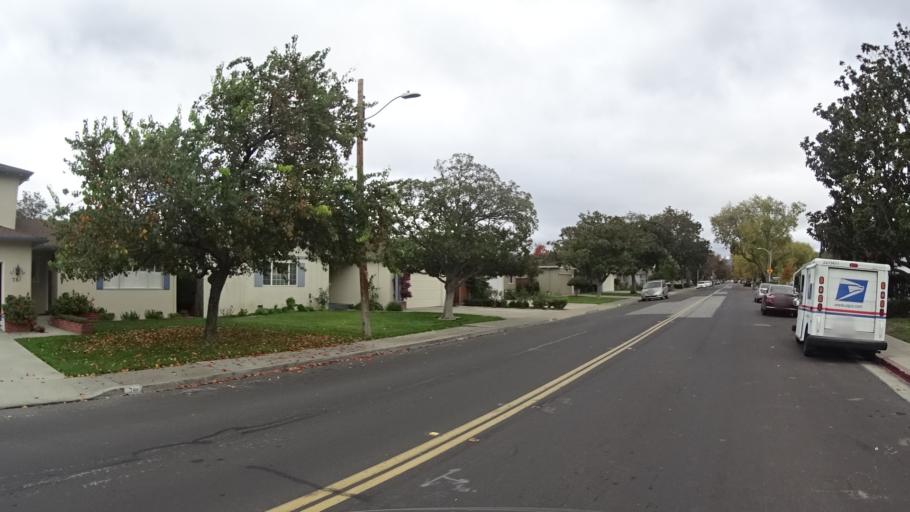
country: US
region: California
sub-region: Santa Clara County
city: Santa Clara
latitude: 37.3367
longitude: -121.9795
